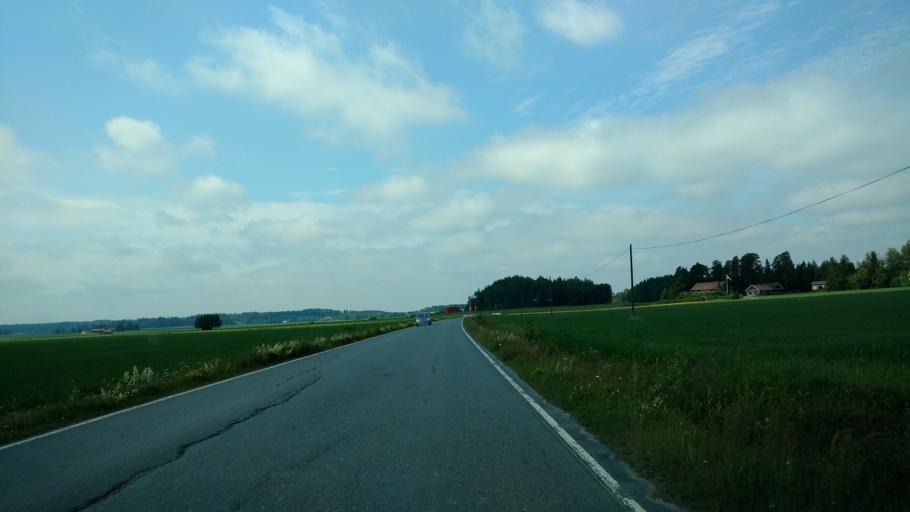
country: FI
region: Haeme
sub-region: Forssa
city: Jokioinen
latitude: 60.7903
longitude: 23.4030
